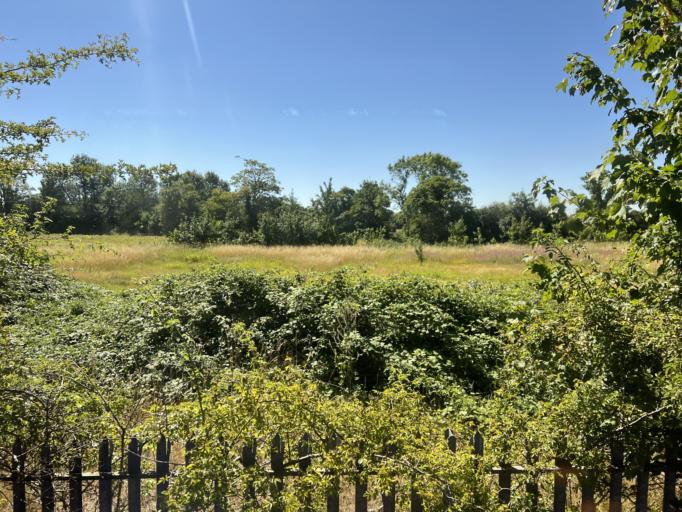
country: GB
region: England
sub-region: Lincolnshire
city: Wainfleet All Saints
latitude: 53.1061
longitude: 0.2325
